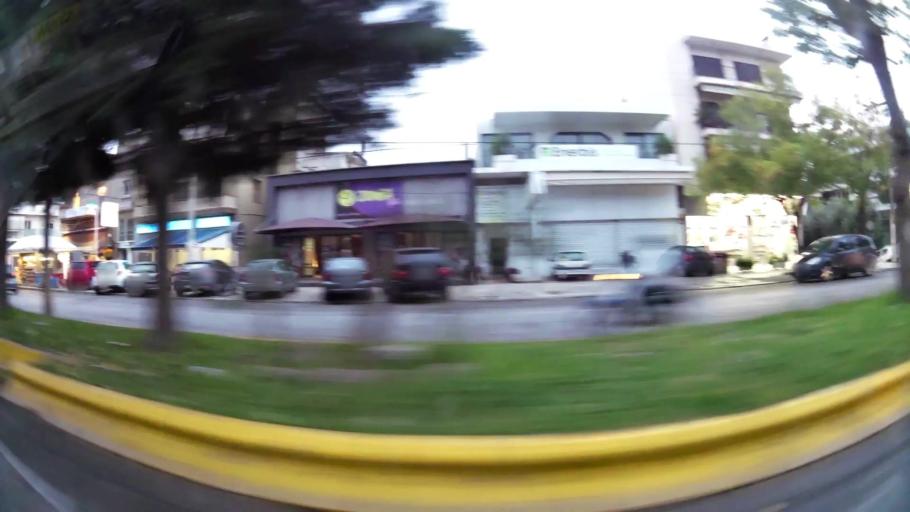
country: GR
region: Attica
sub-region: Nomarchia Athinas
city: Ymittos
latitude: 37.9452
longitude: 23.7477
